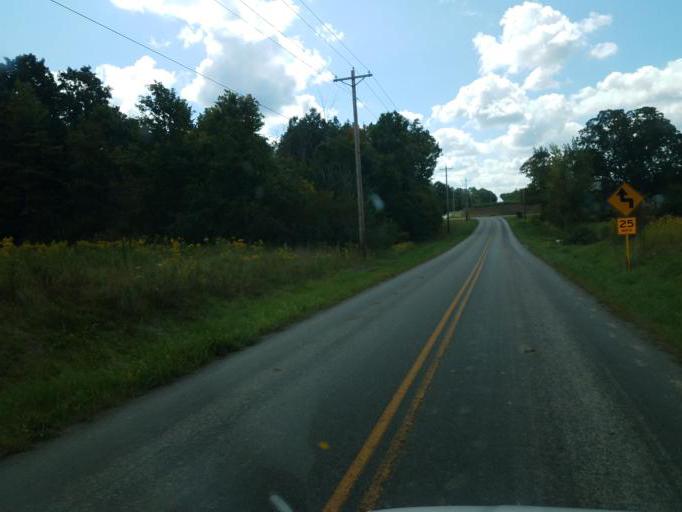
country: US
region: Ohio
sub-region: Wayne County
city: West Salem
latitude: 41.0080
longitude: -82.1270
